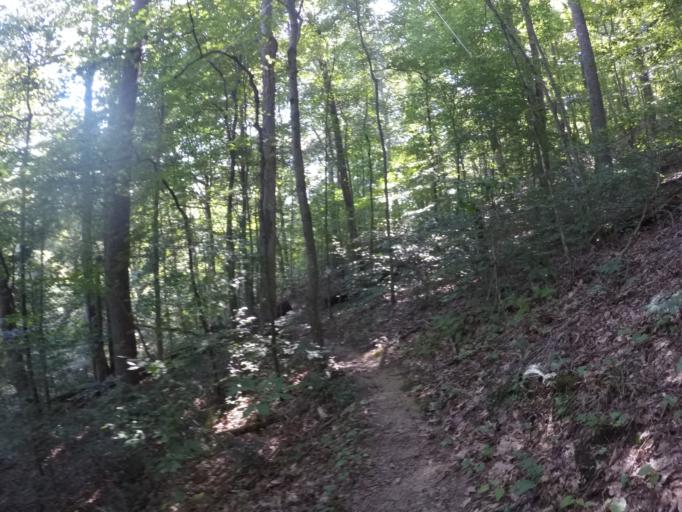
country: US
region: Ohio
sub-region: Lawrence County
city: Ironton
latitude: 38.6259
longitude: -82.6164
